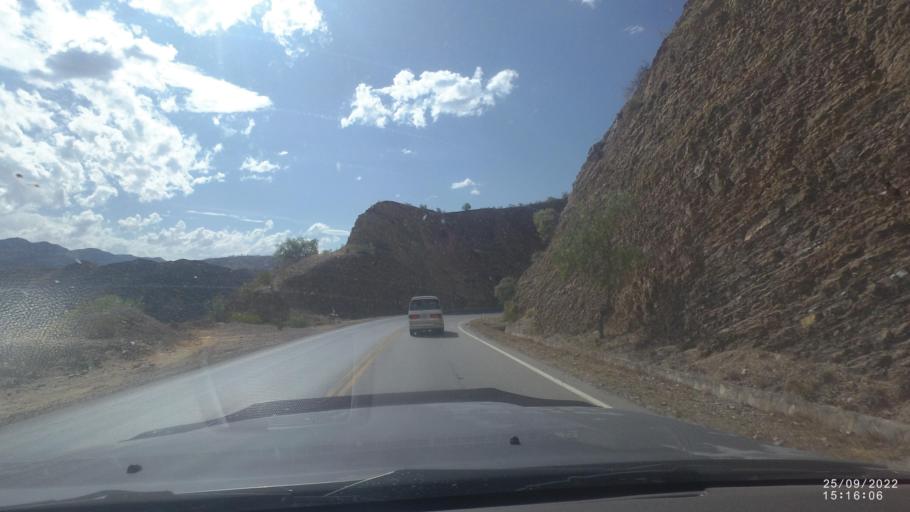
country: BO
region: Cochabamba
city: Irpa Irpa
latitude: -17.6279
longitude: -66.3921
